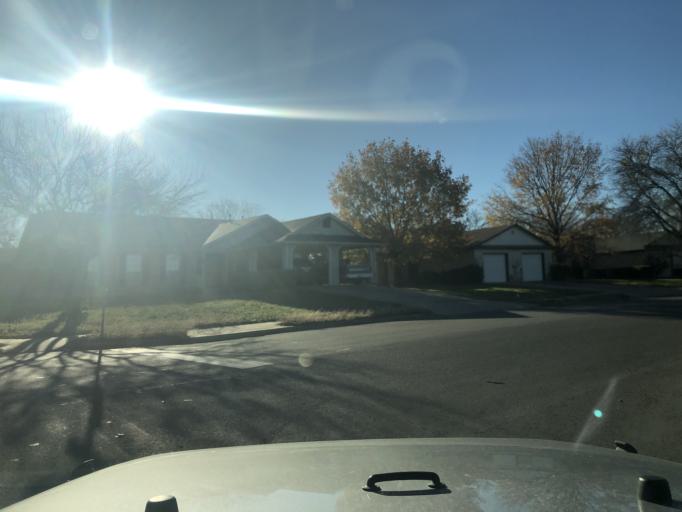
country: US
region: Texas
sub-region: Williamson County
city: Round Rock
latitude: 30.5331
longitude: -97.6777
